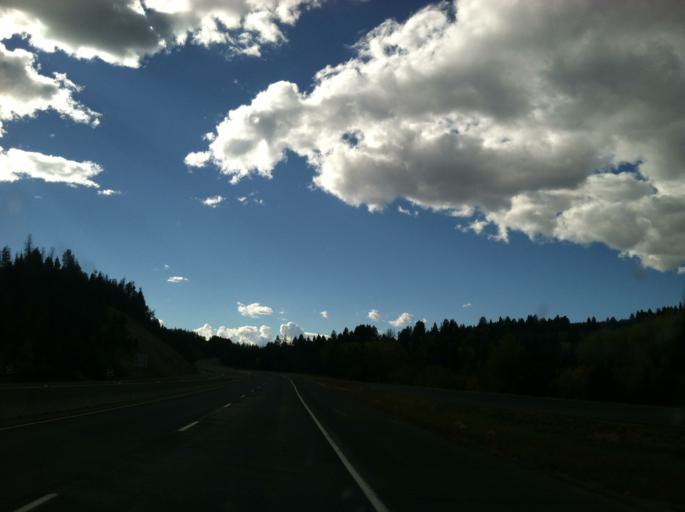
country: US
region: Montana
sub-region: Silver Bow County
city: Butte
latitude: 45.9154
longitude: -112.3787
